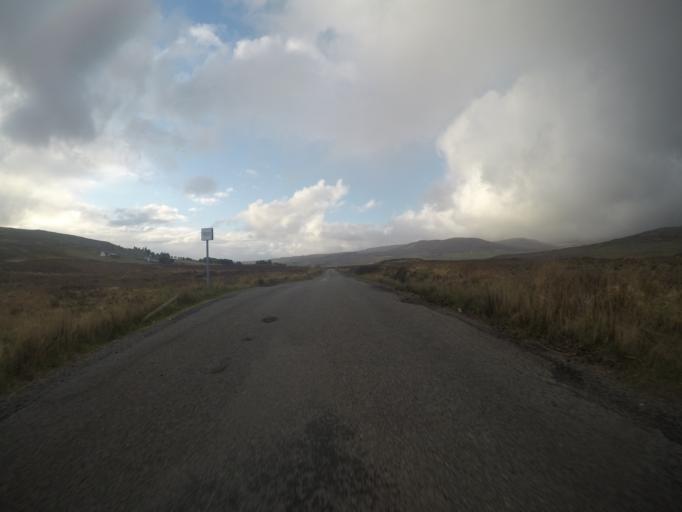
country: GB
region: Scotland
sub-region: Highland
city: Isle of Skye
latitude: 57.4621
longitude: -6.2967
